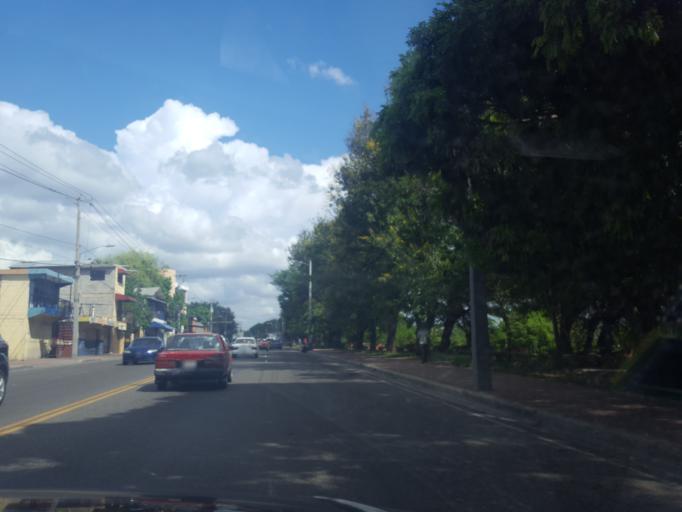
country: DO
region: Santiago
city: Santiago de los Caballeros
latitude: 19.4364
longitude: -70.6977
